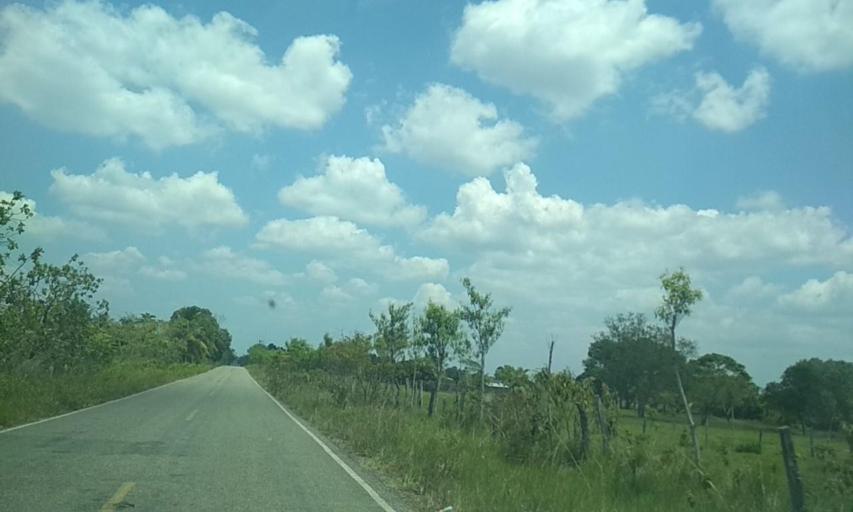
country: MX
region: Tabasco
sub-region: Huimanguillo
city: Huapacal 1ra. Seccion
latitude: 17.7539
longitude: -93.7469
